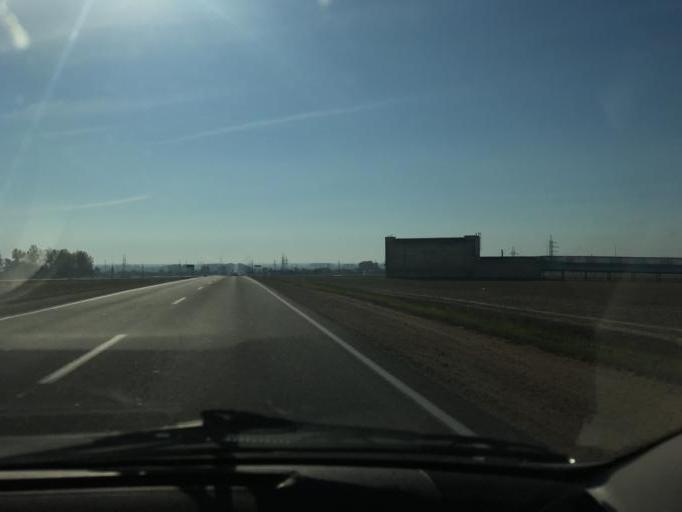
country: BY
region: Minsk
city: Salihorsk
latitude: 52.8581
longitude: 27.4668
